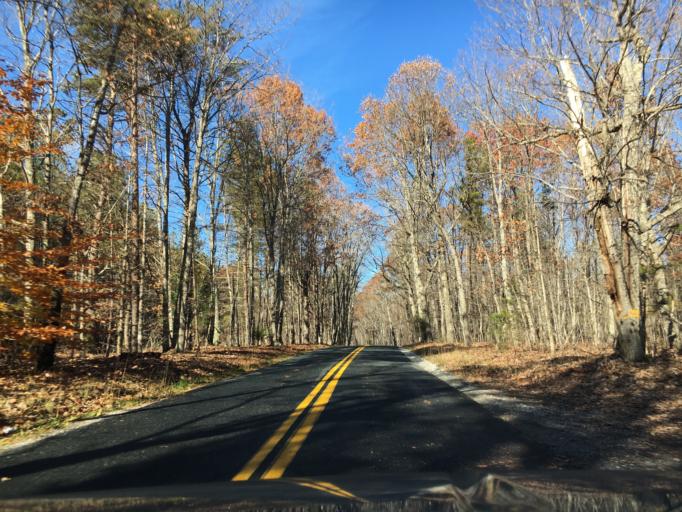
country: US
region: Virginia
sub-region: Buckingham County
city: Buckingham
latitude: 37.4496
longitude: -78.6768
